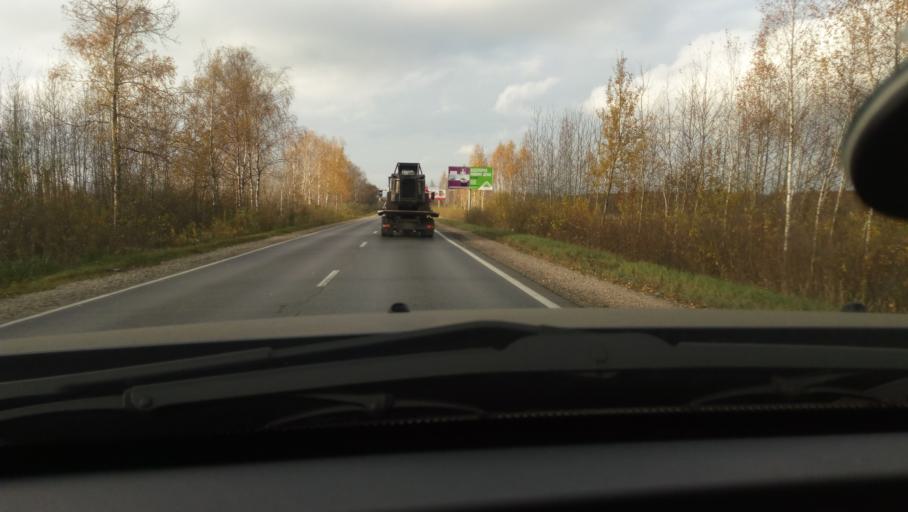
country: RU
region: Moskovskaya
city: Rakhmanovo
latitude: 55.7505
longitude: 38.6185
